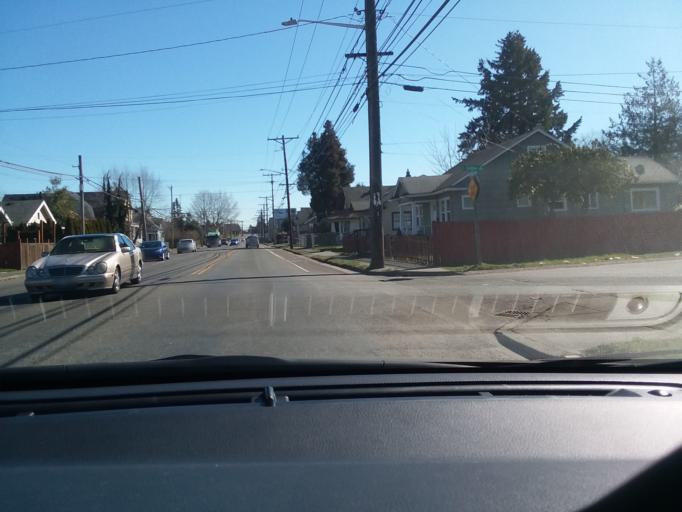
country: US
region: Washington
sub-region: Pierce County
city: Tacoma
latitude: 47.2501
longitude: -122.4671
